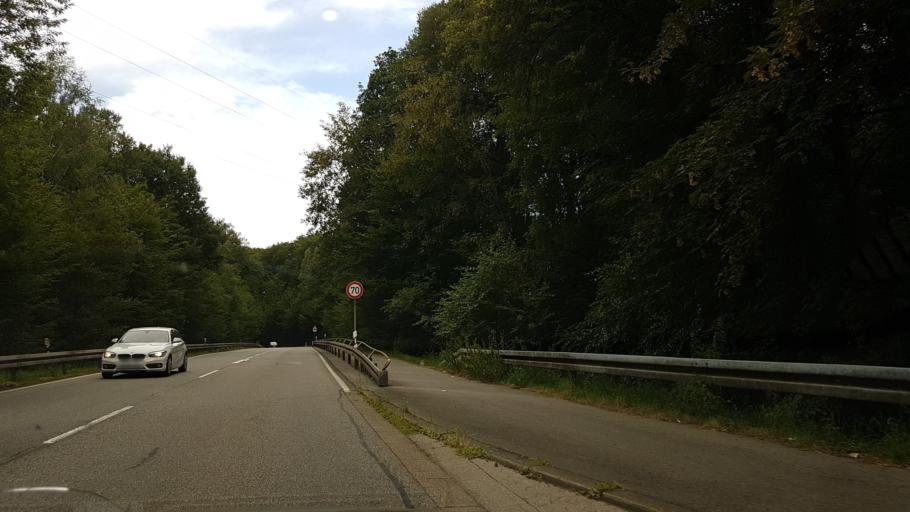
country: DE
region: Saarland
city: Quierschied
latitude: 49.3084
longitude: 7.0524
